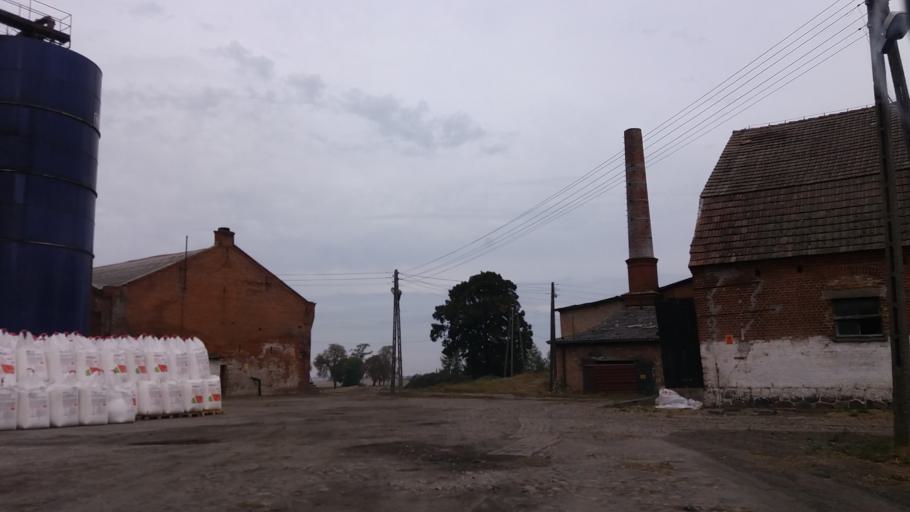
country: PL
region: West Pomeranian Voivodeship
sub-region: Powiat choszczenski
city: Pelczyce
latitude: 53.0917
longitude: 15.3006
